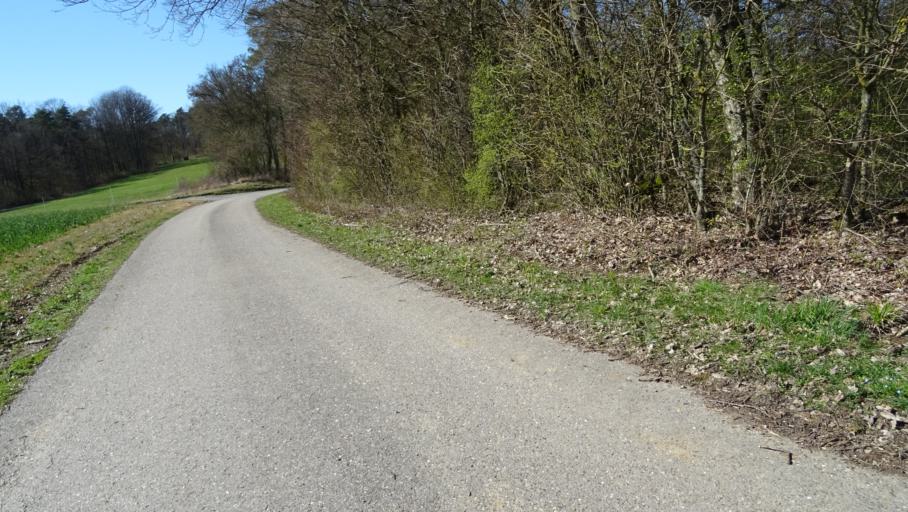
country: DE
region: Baden-Wuerttemberg
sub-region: Karlsruhe Region
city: Seckach
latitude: 49.4284
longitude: 9.3301
